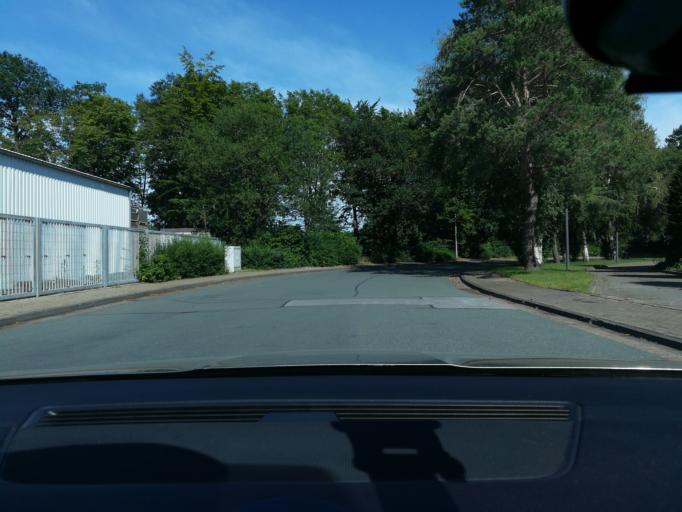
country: DE
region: North Rhine-Westphalia
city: Lubbecke
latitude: 52.3296
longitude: 8.6229
